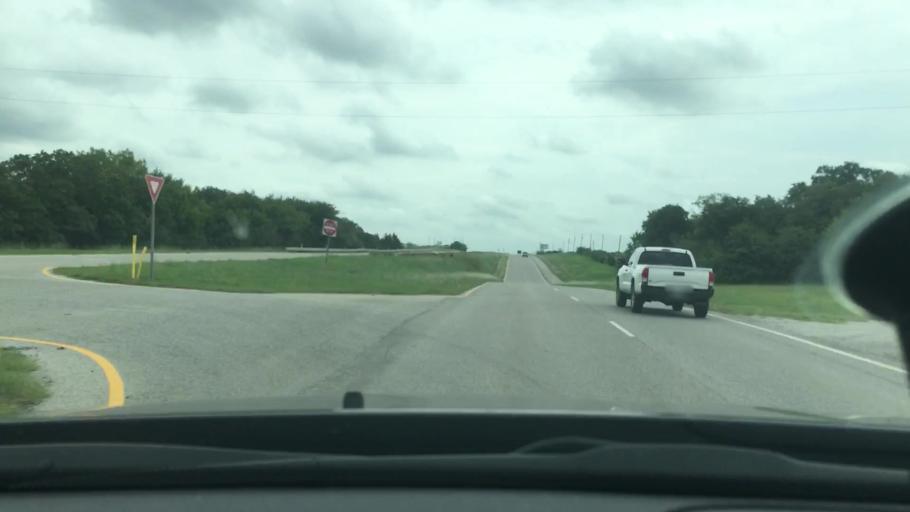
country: US
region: Oklahoma
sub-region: Carter County
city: Wilson
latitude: 34.1729
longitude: -97.4499
